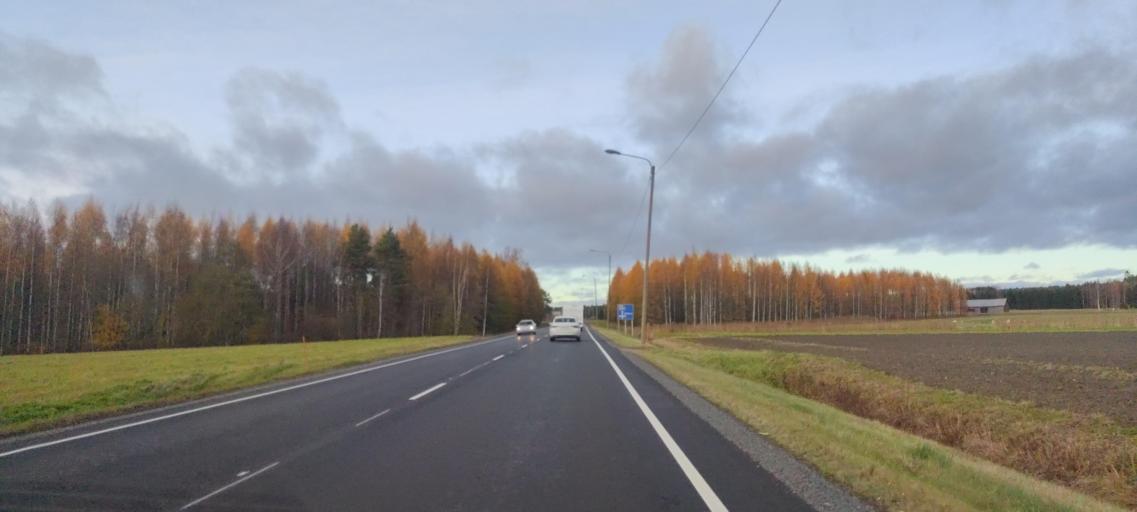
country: FI
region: Satakunta
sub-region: Pori
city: Luvia
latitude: 61.3351
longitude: 21.6592
